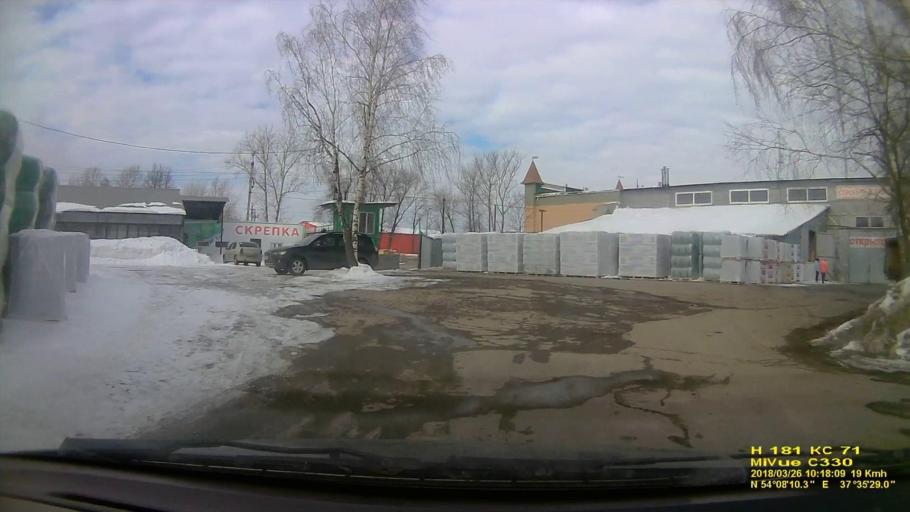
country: RU
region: Tula
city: Mendeleyevskiy
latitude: 54.1360
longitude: 37.5932
